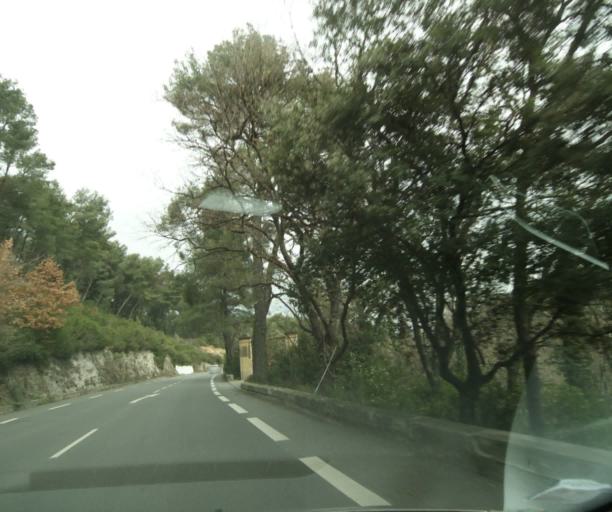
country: FR
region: Provence-Alpes-Cote d'Azur
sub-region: Departement des Bouches-du-Rhone
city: Aix-en-Provence
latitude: 43.5462
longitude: 5.4606
